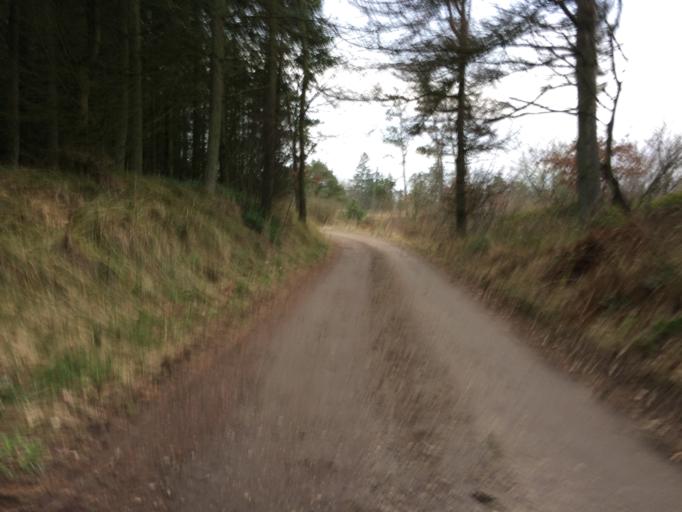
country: DK
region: Central Jutland
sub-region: Holstebro Kommune
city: Ulfborg
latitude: 56.2644
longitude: 8.2476
